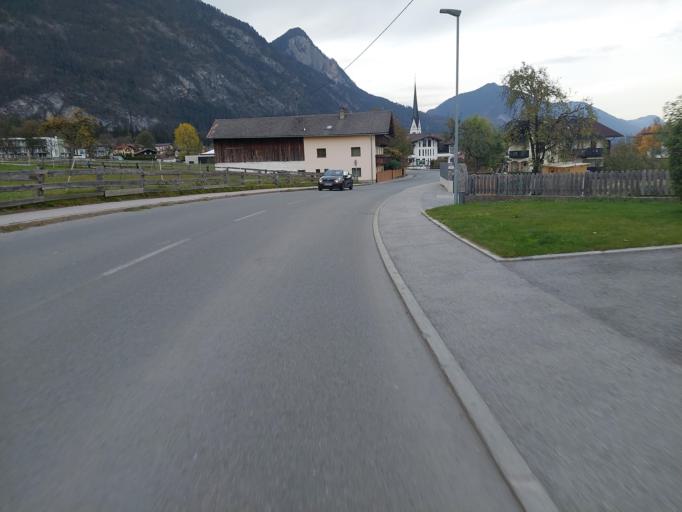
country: AT
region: Tyrol
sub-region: Politischer Bezirk Kufstein
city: Munster
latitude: 47.4183
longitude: 11.8319
